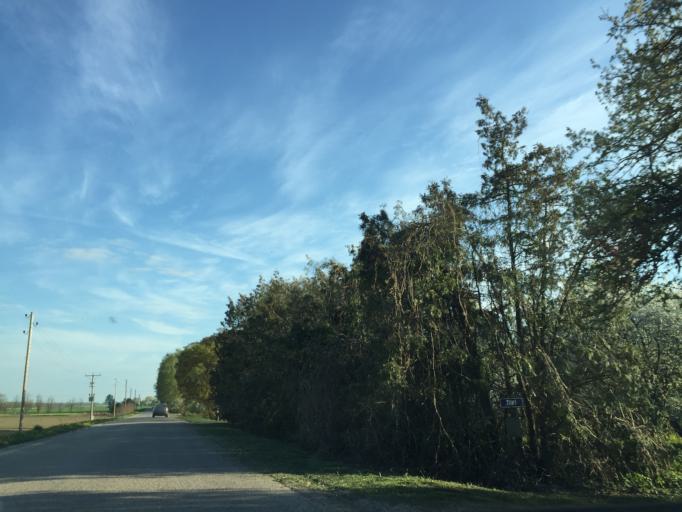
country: LV
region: Bauskas Rajons
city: Bauska
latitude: 56.3060
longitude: 24.2611
